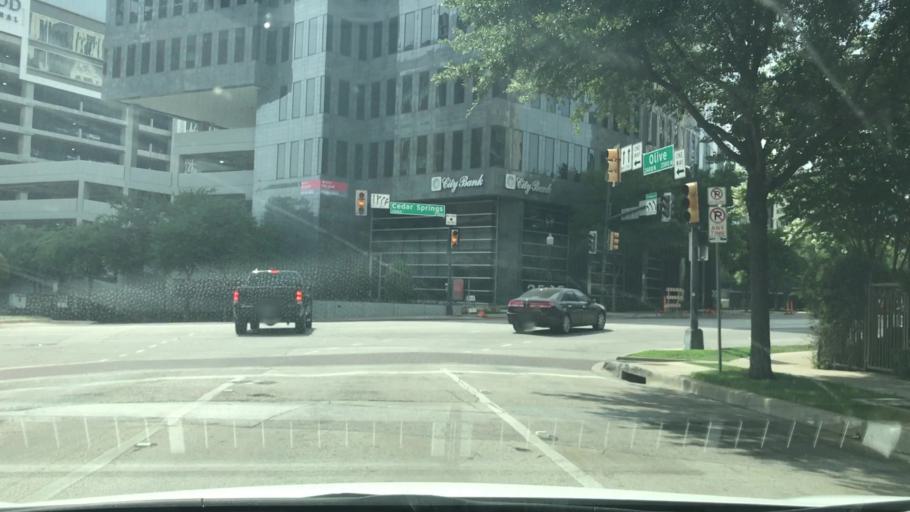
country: US
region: Texas
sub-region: Dallas County
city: Dallas
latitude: 32.7919
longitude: -96.8048
